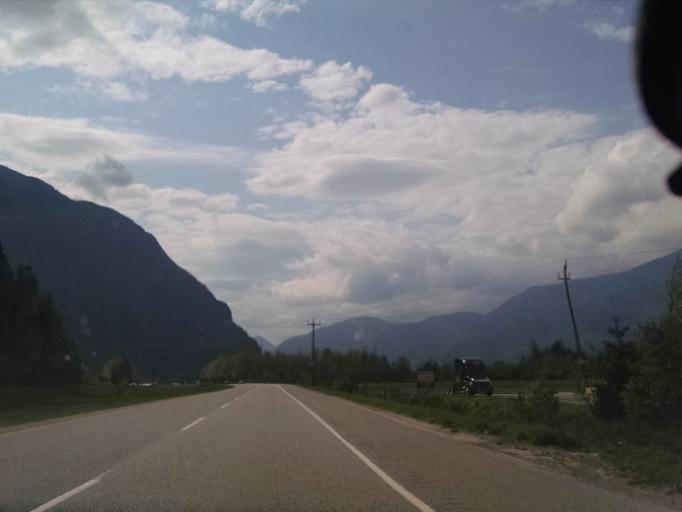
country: CA
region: British Columbia
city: Hope
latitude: 49.3648
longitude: -121.4841
